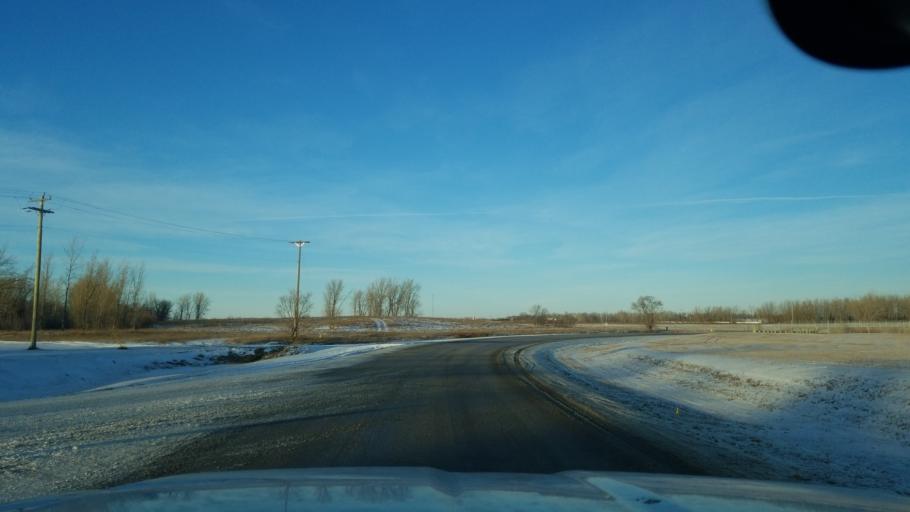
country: CA
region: Manitoba
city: Portage la Prairie
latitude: 49.9477
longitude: -98.3390
